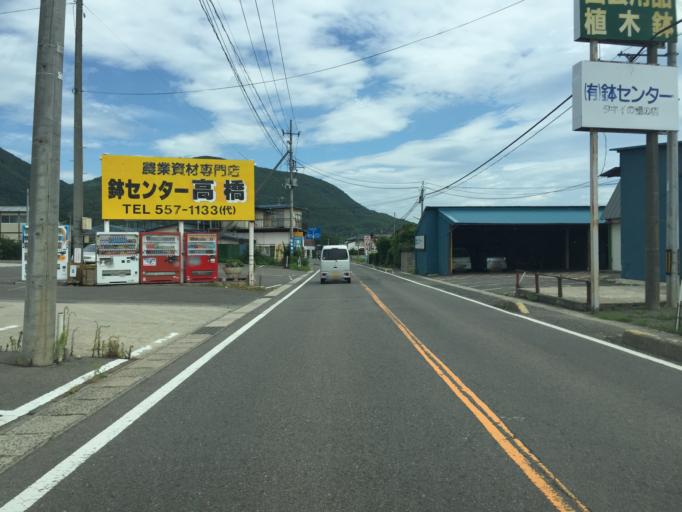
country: JP
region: Fukushima
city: Fukushima-shi
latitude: 37.7964
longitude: 140.4011
